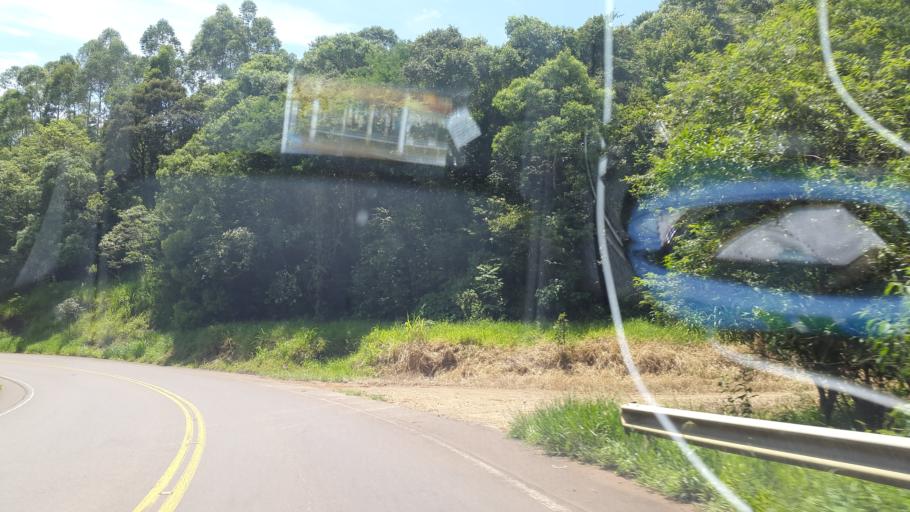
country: BR
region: Rio Grande do Sul
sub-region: Frederico Westphalen
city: Frederico Westphalen
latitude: -27.0668
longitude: -53.4671
